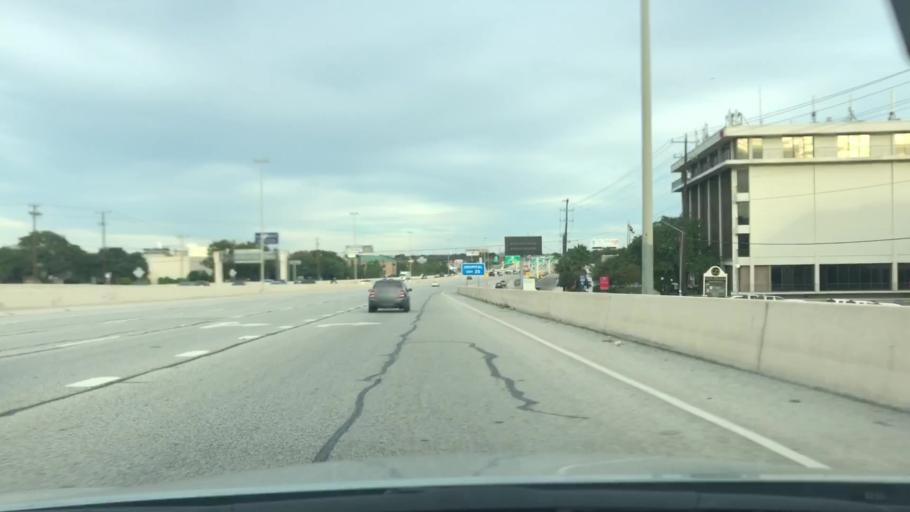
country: US
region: Texas
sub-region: Bexar County
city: Alamo Heights
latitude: 29.5155
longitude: -98.4363
